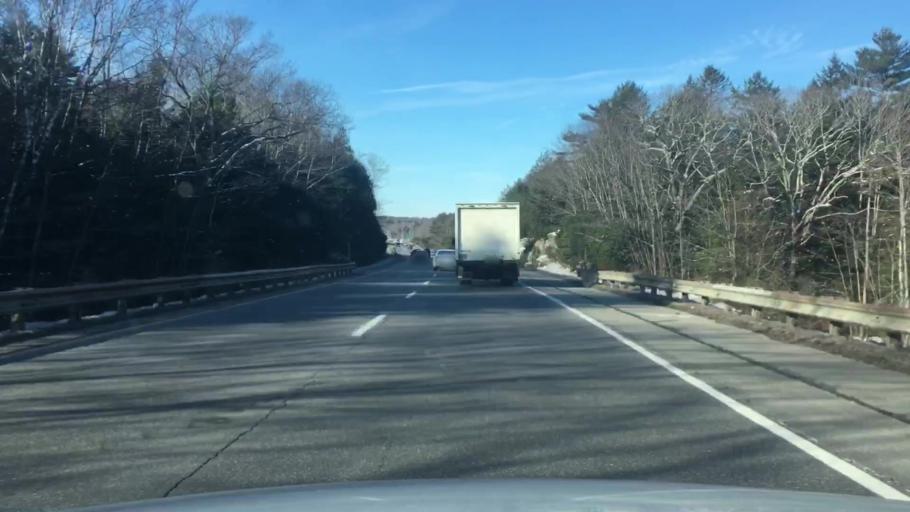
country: US
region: Maine
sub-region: Sagadahoc County
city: Bath
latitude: 43.9149
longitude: -69.8504
